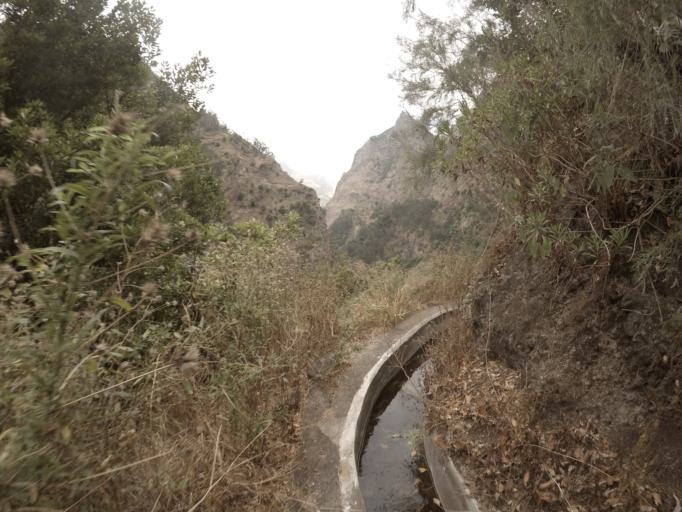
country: PT
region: Madeira
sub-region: Camara de Lobos
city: Curral das Freiras
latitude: 32.6938
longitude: -16.9655
